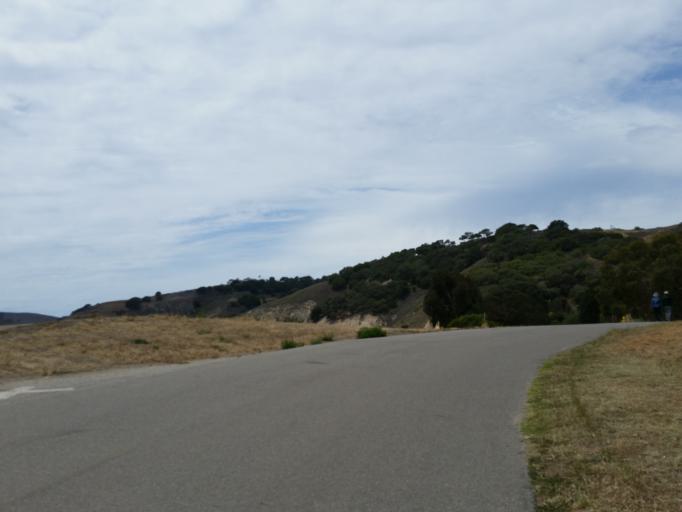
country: US
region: California
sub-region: San Luis Obispo County
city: Avila Beach
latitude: 35.1831
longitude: -120.7292
